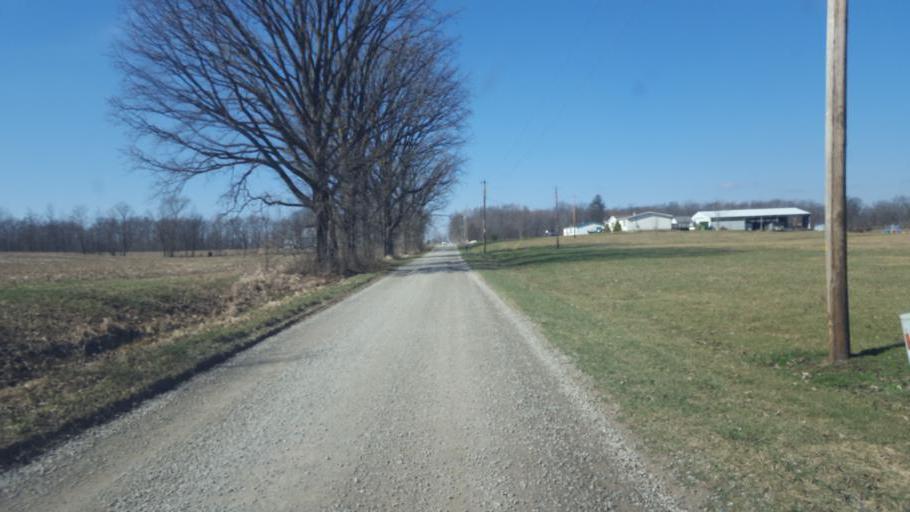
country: US
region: Ohio
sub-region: Morrow County
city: Mount Gilead
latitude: 40.5065
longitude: -82.7561
